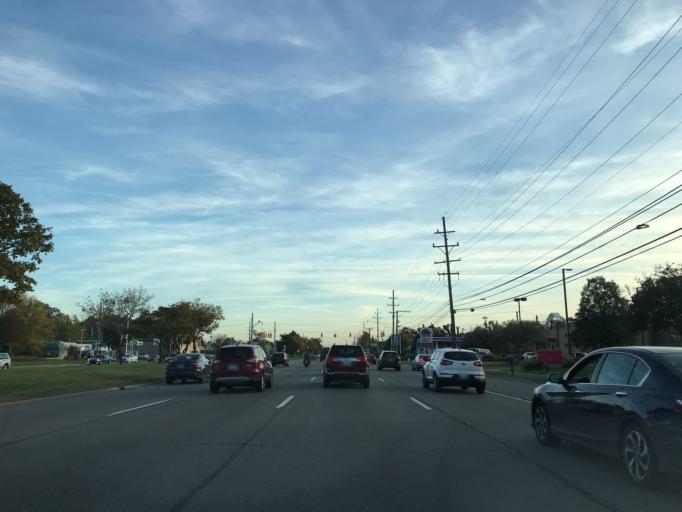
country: US
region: Michigan
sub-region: Oakland County
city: Bingham Farms
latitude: 42.4588
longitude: -83.2788
